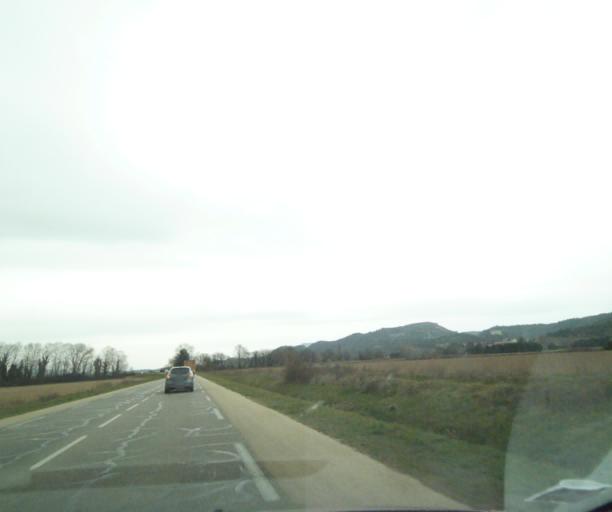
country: FR
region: Provence-Alpes-Cote d'Azur
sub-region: Departement des Bouches-du-Rhone
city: Meyrargues
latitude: 43.6518
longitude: 5.5192
